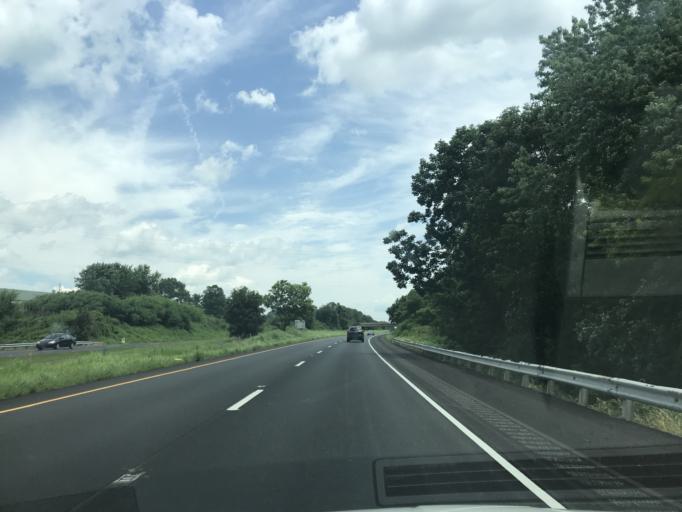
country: US
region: Pennsylvania
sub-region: Chester County
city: West Grove
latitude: 39.8252
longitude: -75.8963
